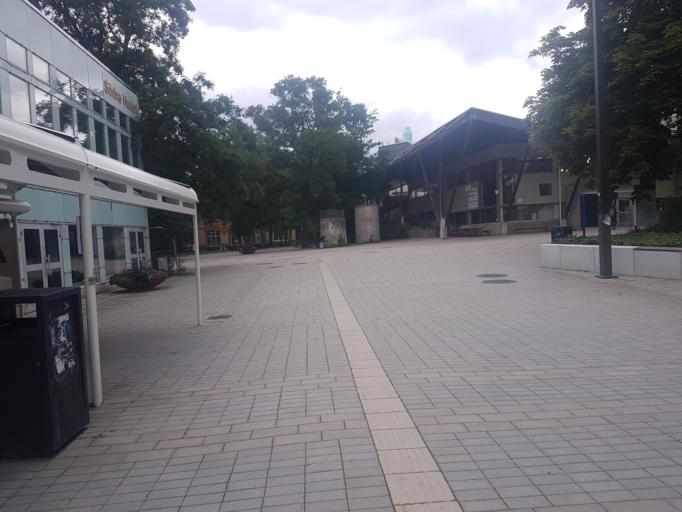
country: SE
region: Stockholm
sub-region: Norrtalje Kommun
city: Bergshamra
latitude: 59.3633
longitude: 18.0589
